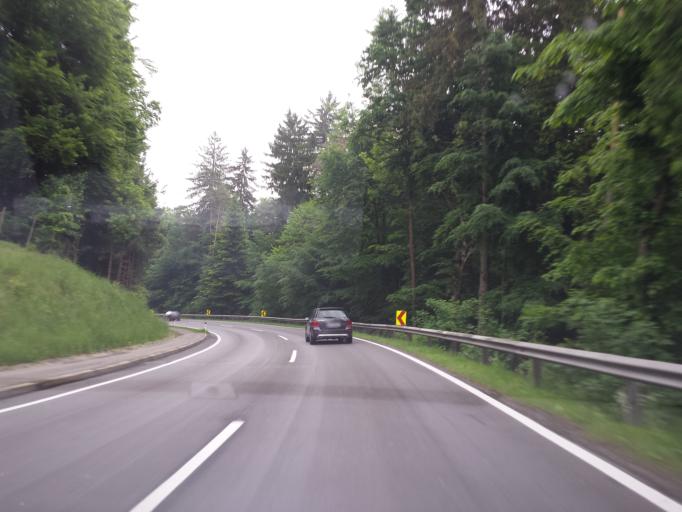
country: AT
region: Styria
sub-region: Politischer Bezirk Weiz
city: Anger
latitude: 47.2497
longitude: 15.7038
